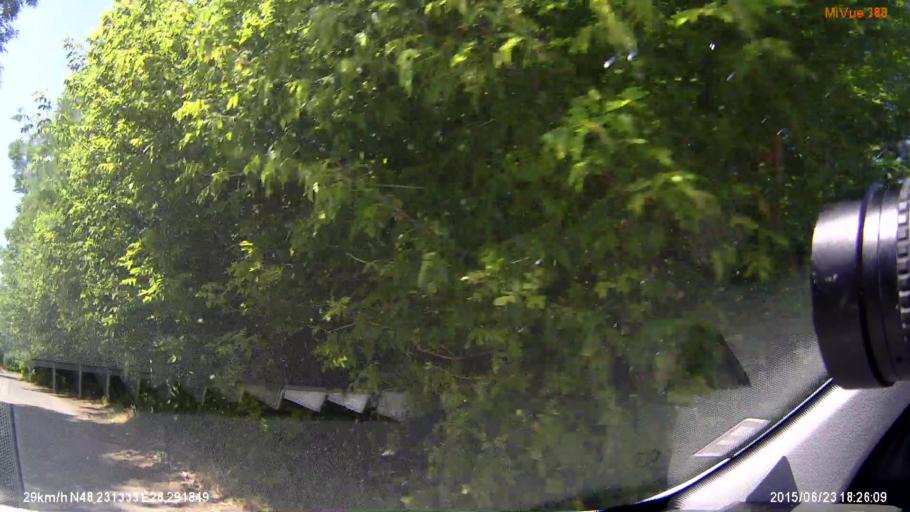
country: UA
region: Vinnyts'ka
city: Yampil'
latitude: 48.2315
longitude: 28.2920
